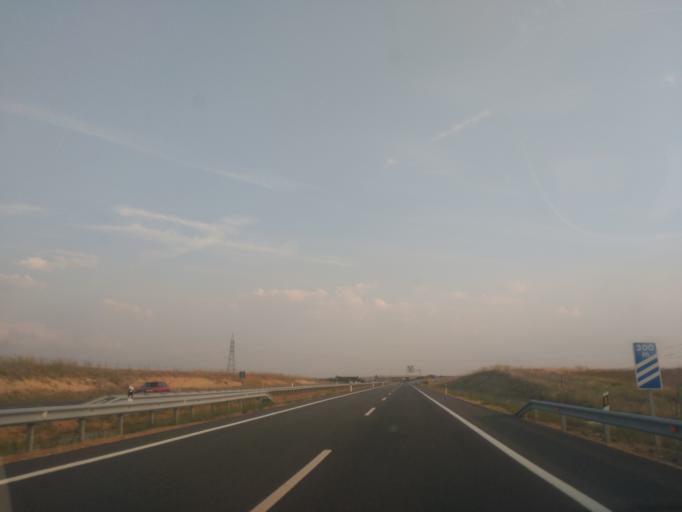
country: ES
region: Castille and Leon
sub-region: Provincia de Zamora
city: Roales
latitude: 41.5842
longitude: -5.7771
